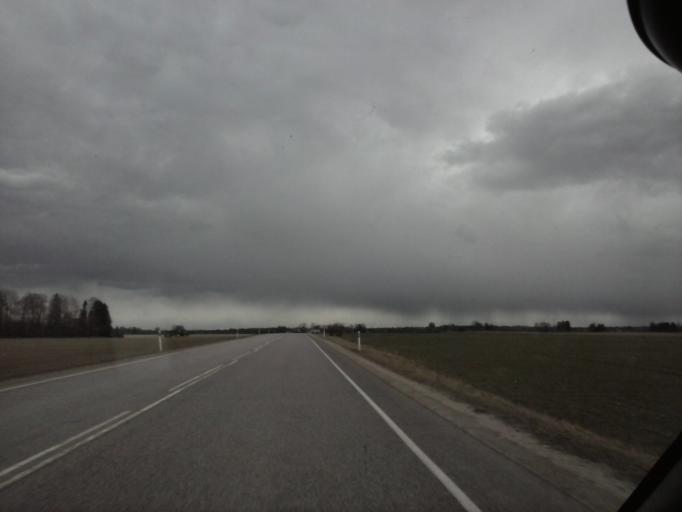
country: EE
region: Jogevamaa
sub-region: Poltsamaa linn
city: Poltsamaa
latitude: 58.7439
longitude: 25.7823
